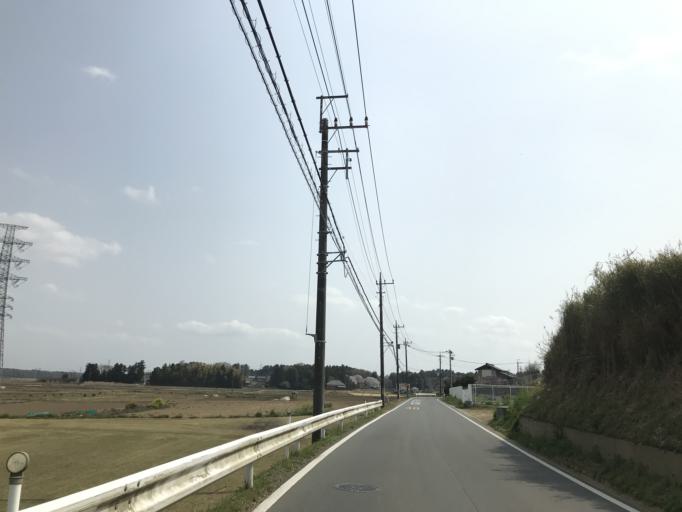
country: JP
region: Ibaraki
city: Ushiku
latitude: 36.0088
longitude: 140.0658
